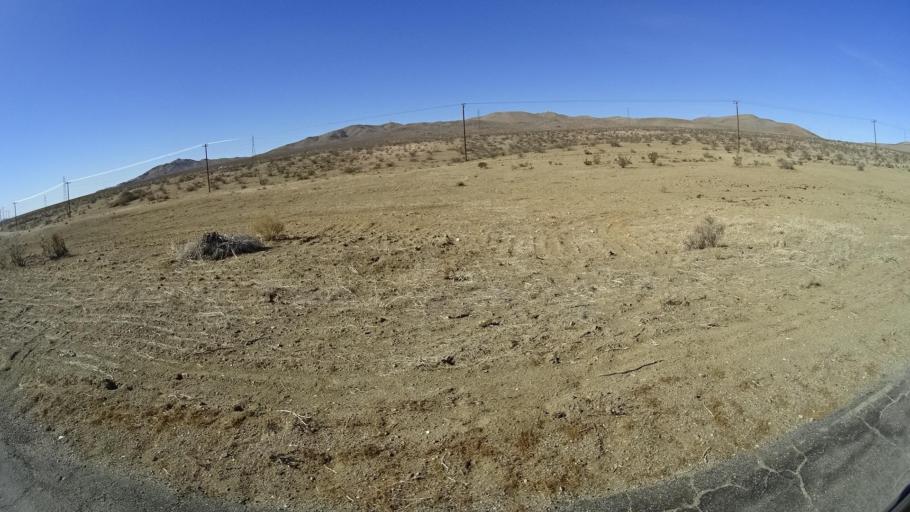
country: US
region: California
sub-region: Kern County
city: Ridgecrest
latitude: 35.3369
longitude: -117.6316
